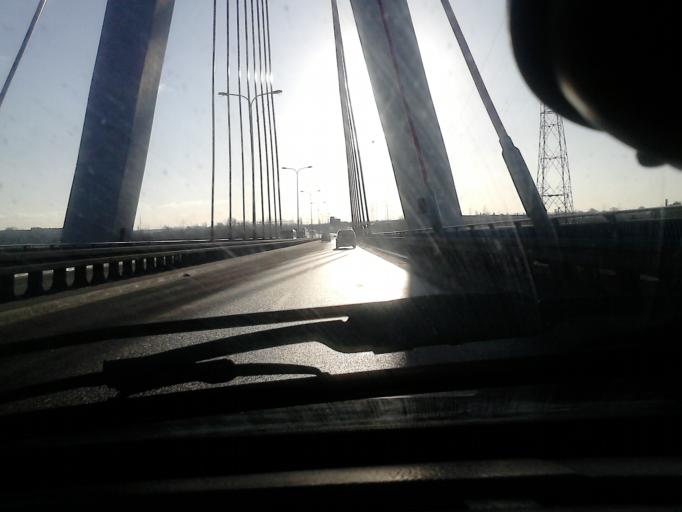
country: PL
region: Pomeranian Voivodeship
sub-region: Gdansk
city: Gdansk
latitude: 54.3559
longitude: 18.6943
